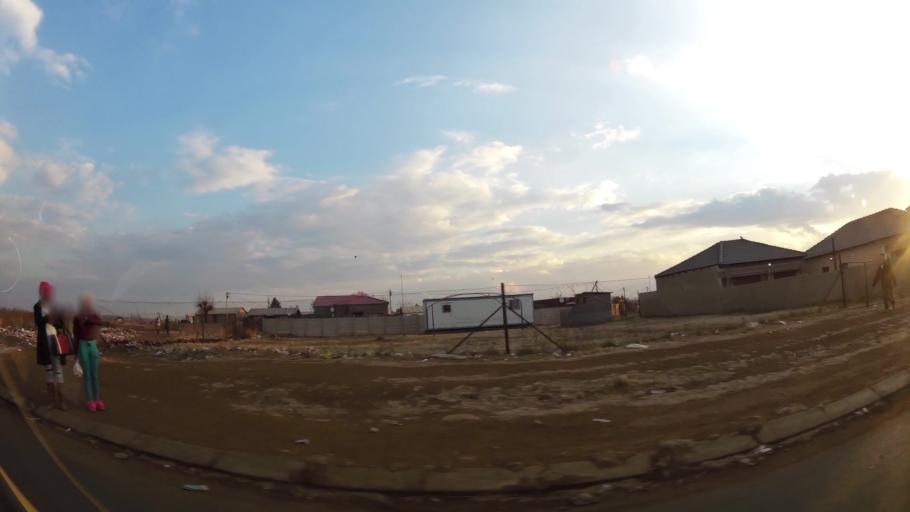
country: ZA
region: Gauteng
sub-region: City of Johannesburg Metropolitan Municipality
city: Orange Farm
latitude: -26.5494
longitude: 27.8823
